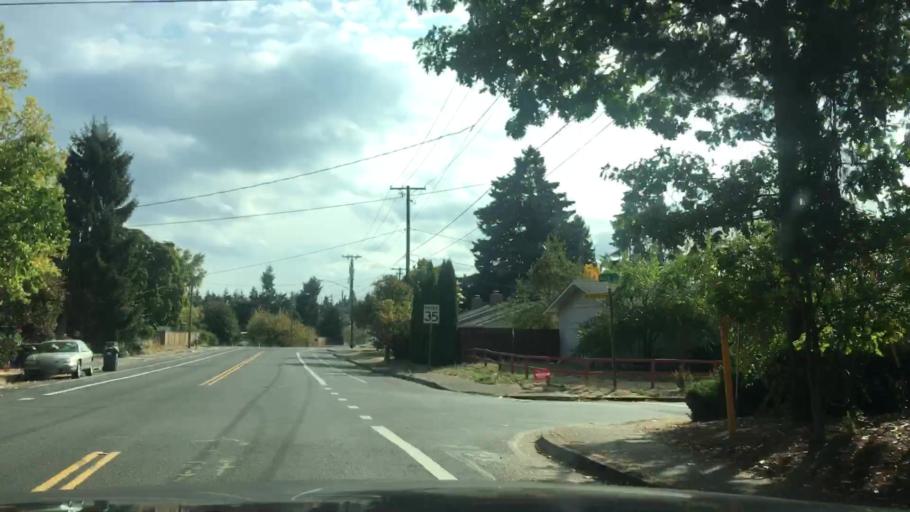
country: US
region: Oregon
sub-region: Lane County
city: Eugene
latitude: 44.0919
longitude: -123.0877
